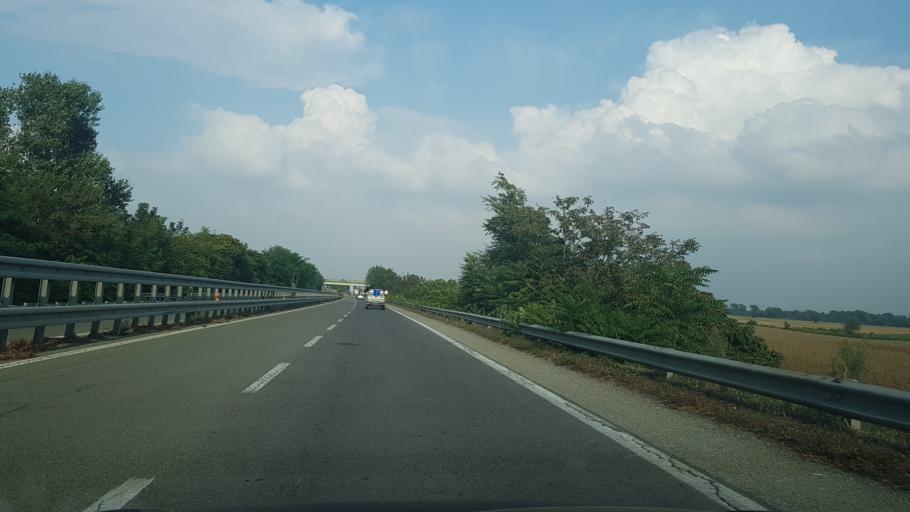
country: IT
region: Piedmont
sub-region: Provincia di Alessandria
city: Alessandria
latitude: 44.8841
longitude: 8.6097
